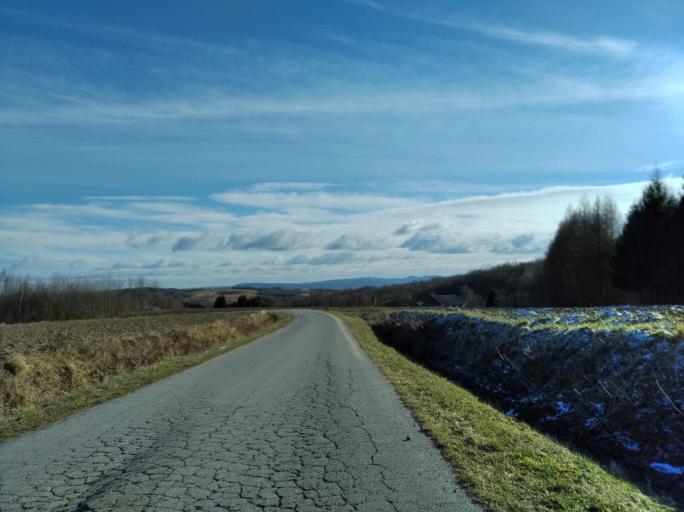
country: PL
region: Subcarpathian Voivodeship
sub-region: Powiat strzyzowski
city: Wisniowa
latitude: 49.9050
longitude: 21.6517
